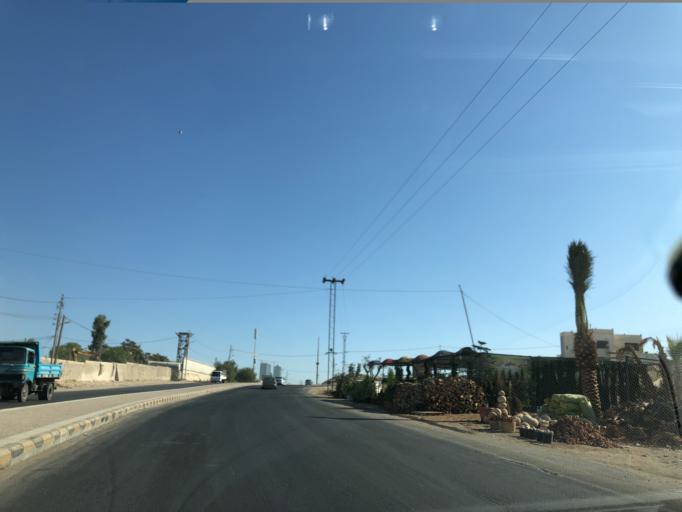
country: JO
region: Amman
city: Wadi as Sir
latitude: 31.9350
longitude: 35.8478
